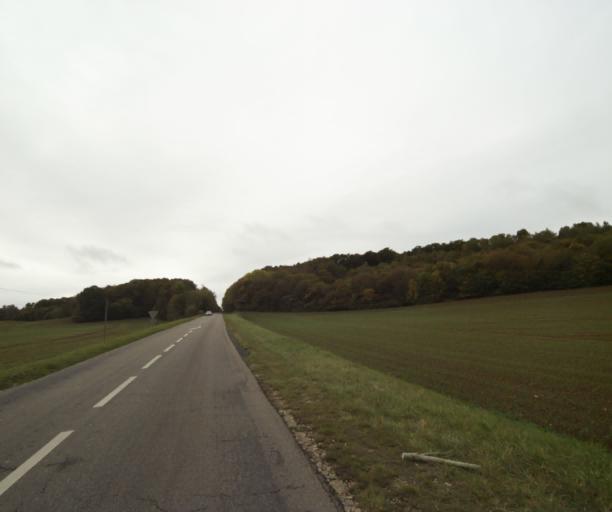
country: FR
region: Centre
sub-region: Departement d'Eure-et-Loir
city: Dreux
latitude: 48.7708
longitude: 1.3704
